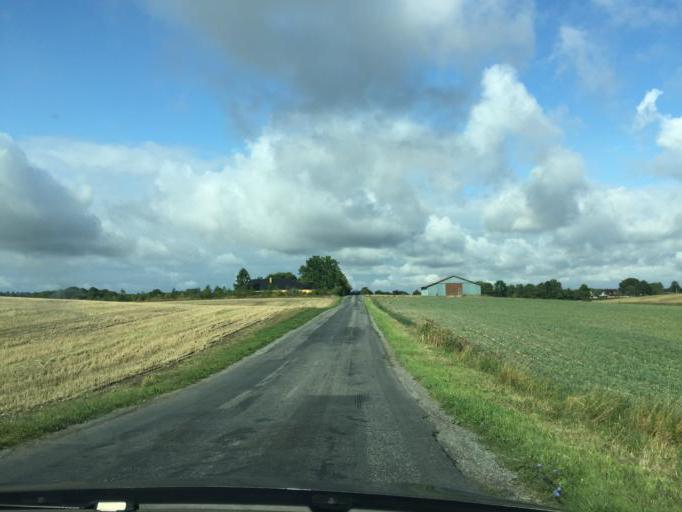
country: DK
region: South Denmark
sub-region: Faaborg-Midtfyn Kommune
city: Faaborg
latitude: 55.1959
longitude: 10.2621
